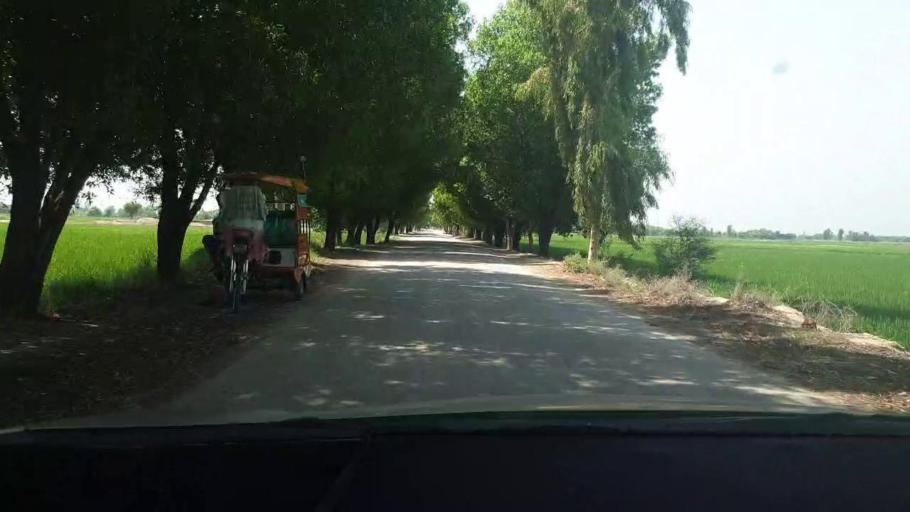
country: PK
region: Sindh
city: Miro Khan
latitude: 27.6718
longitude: 68.0575
